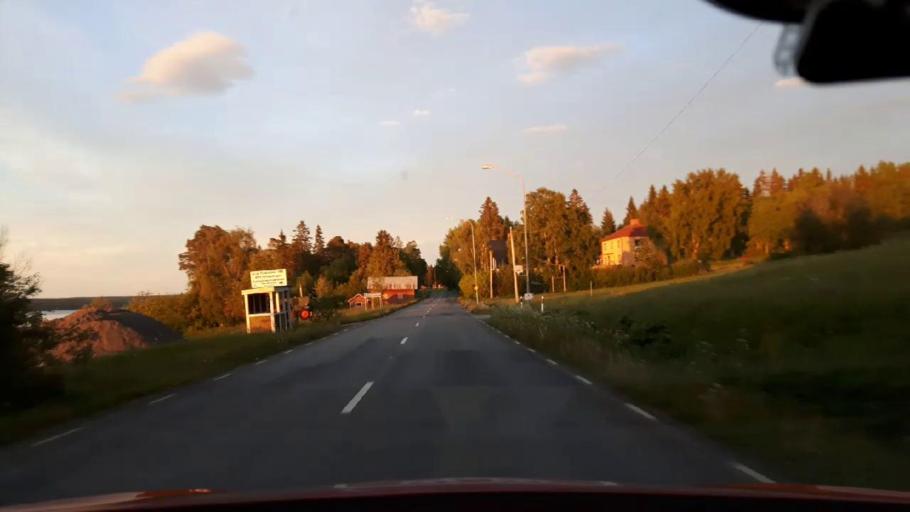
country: SE
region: Jaemtland
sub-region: OEstersunds Kommun
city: Ostersund
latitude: 63.1338
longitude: 14.6495
